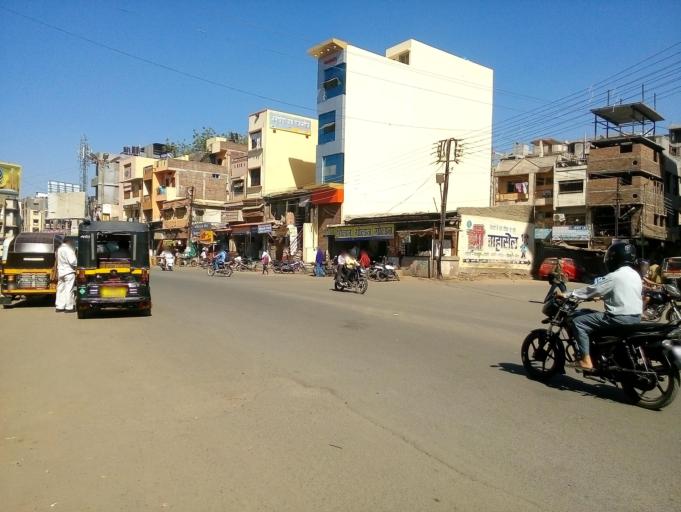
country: IN
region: Maharashtra
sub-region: Aurangabad Division
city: Aurangabad
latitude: 19.8840
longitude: 75.3266
